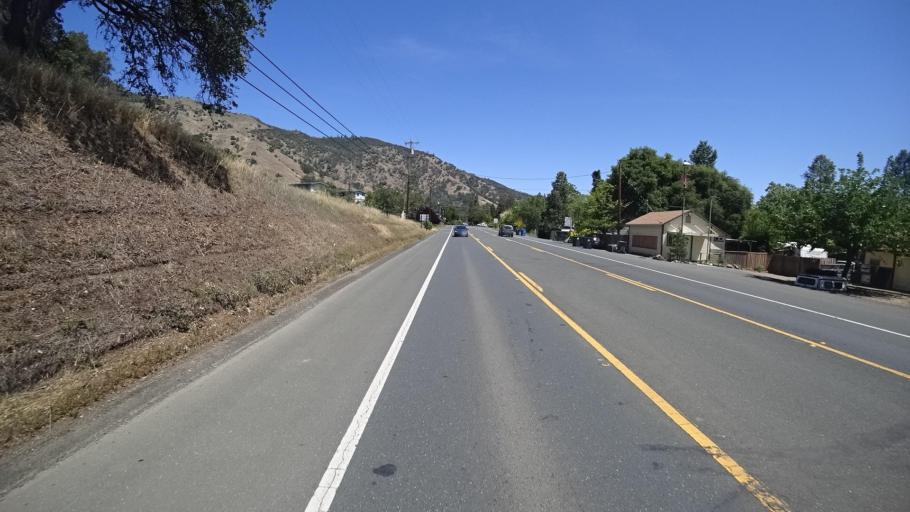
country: US
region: California
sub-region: Lake County
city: Nice
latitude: 39.1230
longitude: -122.8497
